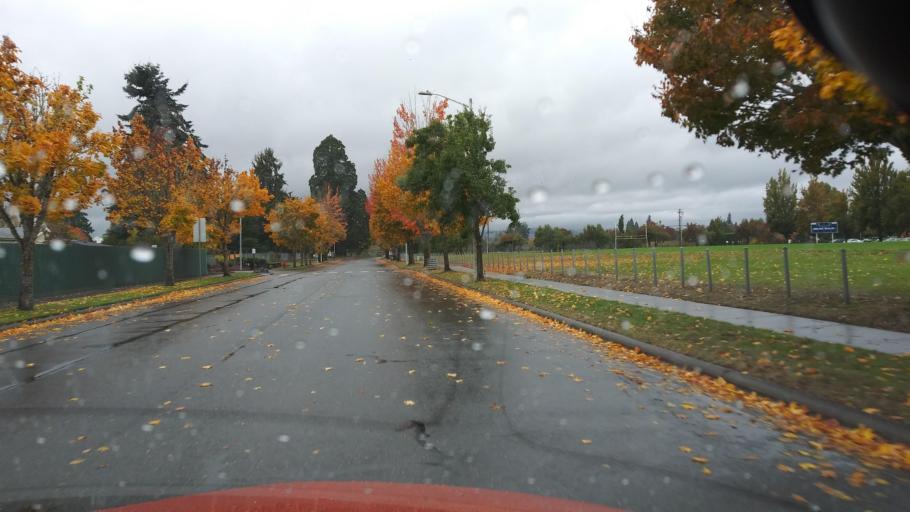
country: US
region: Oregon
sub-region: Washington County
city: Cornelius
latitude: 45.5140
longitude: -123.0732
